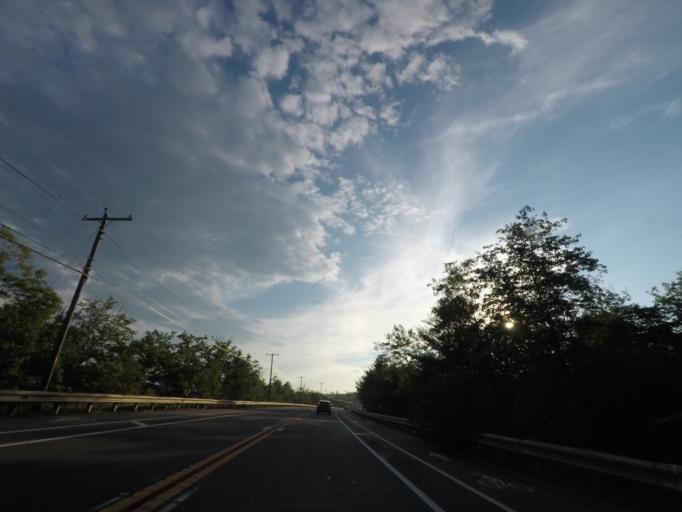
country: US
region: Massachusetts
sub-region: Worcester County
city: Fiskdale
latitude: 42.1108
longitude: -72.1397
